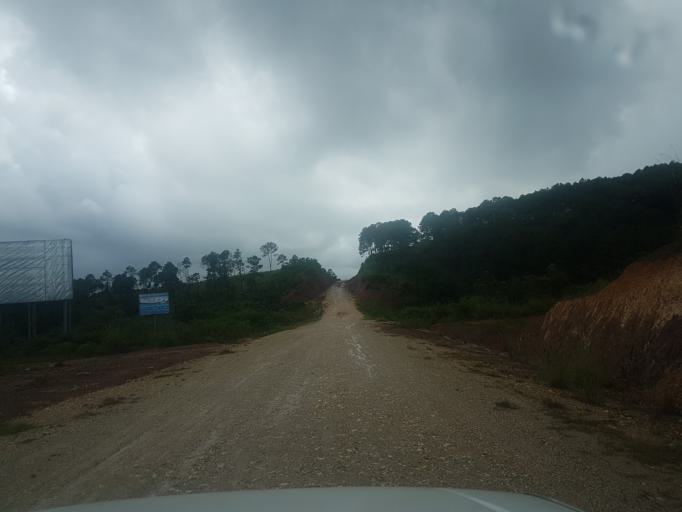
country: LA
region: Xiangkhoang
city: Muang Phonsavan
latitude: 19.4897
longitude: 103.2653
